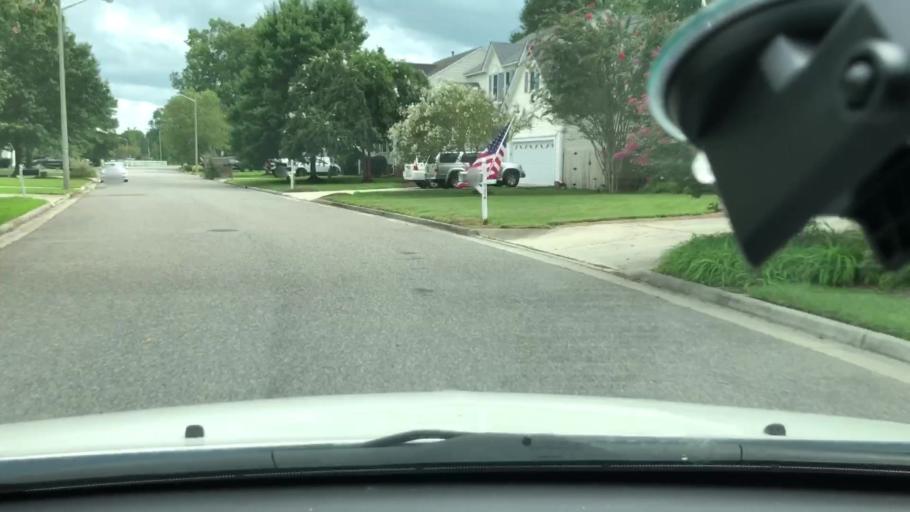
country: US
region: Virginia
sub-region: City of Chesapeake
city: Chesapeake
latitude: 36.7172
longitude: -76.2816
